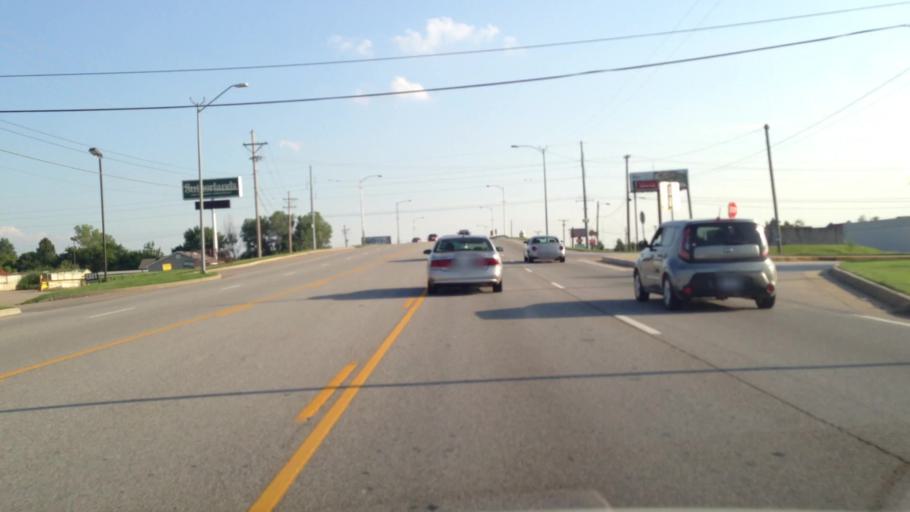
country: US
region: Missouri
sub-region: Jasper County
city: Duquesne
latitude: 37.0601
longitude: -94.4771
